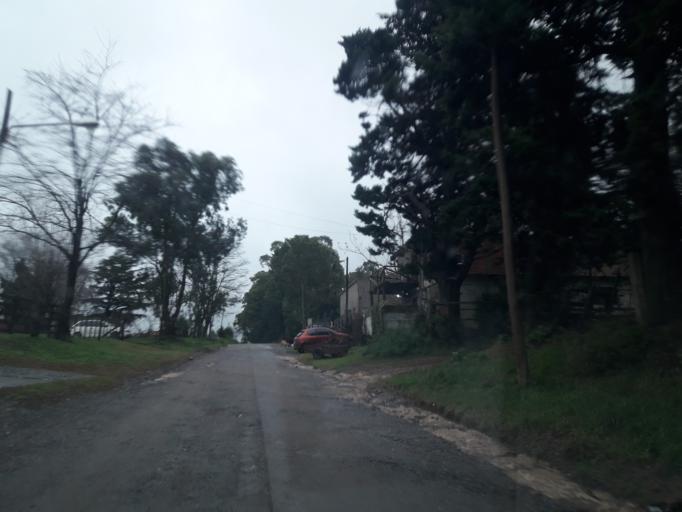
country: AR
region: Buenos Aires
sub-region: Partido de Tandil
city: Tandil
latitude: -37.3303
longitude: -59.1785
